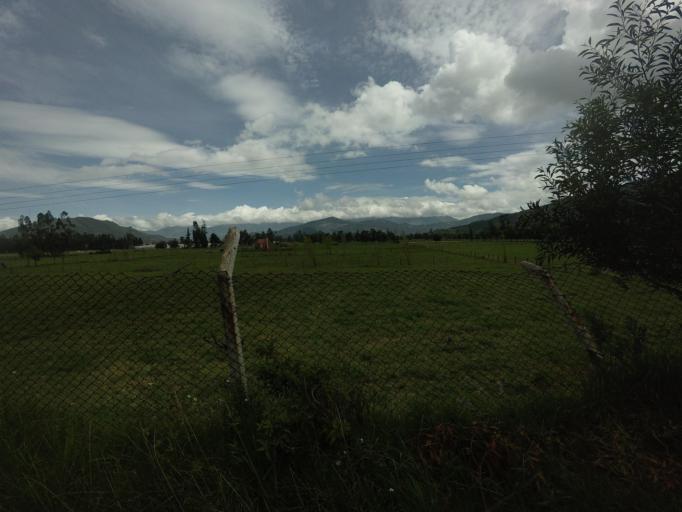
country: CO
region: Boyaca
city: Nobsa
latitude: 5.7811
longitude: -72.9747
